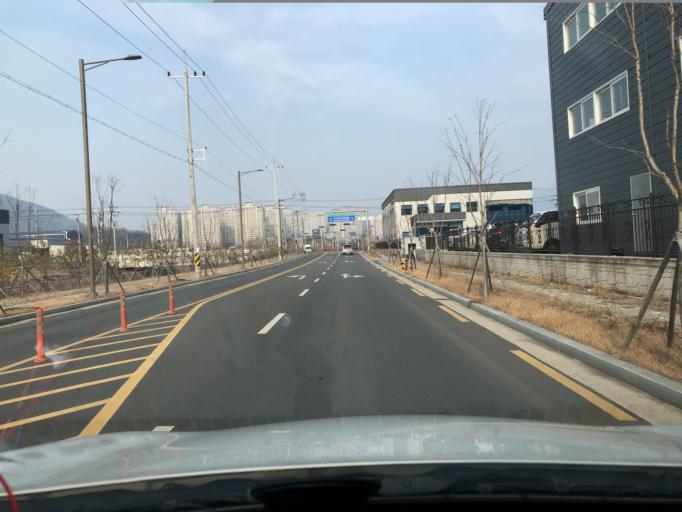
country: KR
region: Gyeongsangnam-do
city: Changnyeong
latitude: 35.6476
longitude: 128.4085
